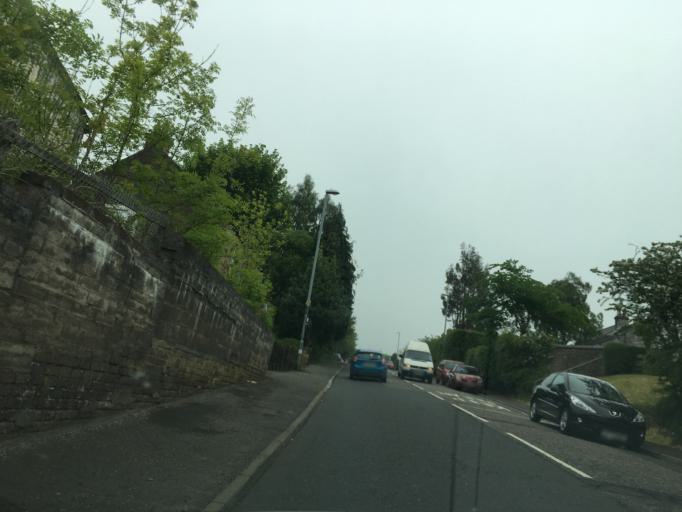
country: GB
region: Scotland
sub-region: Midlothian
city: Penicuik
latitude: 55.8460
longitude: -3.1926
